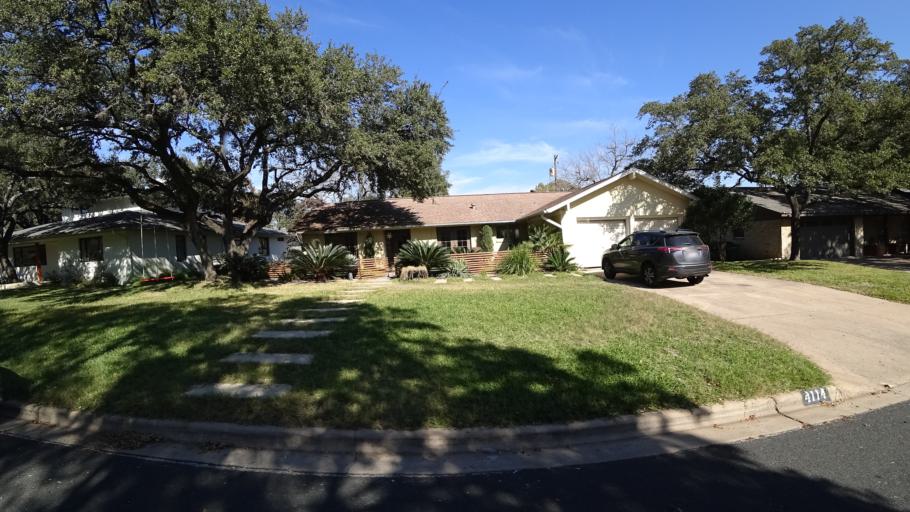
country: US
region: Texas
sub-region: Williamson County
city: Jollyville
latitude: 30.3678
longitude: -97.7625
